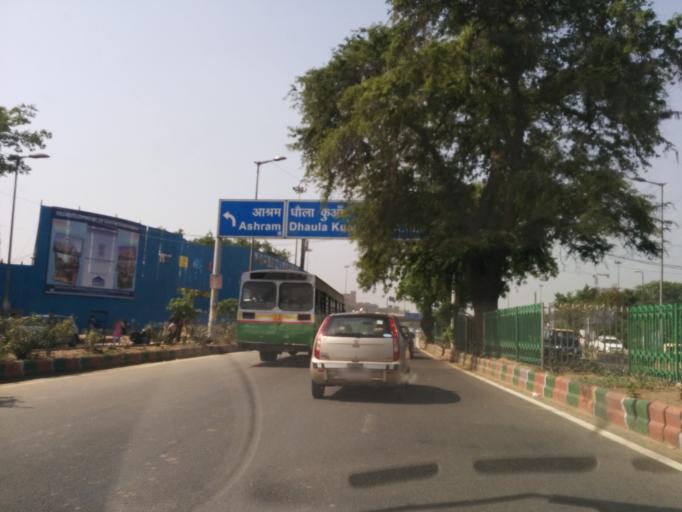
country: IN
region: NCT
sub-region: New Delhi
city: New Delhi
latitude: 28.5730
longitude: 77.2094
